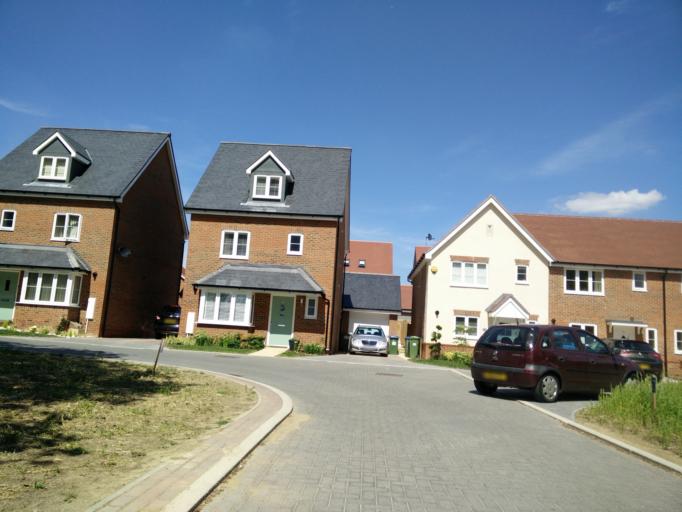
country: GB
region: England
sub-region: West Sussex
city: Horsham
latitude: 51.0655
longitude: -0.3614
